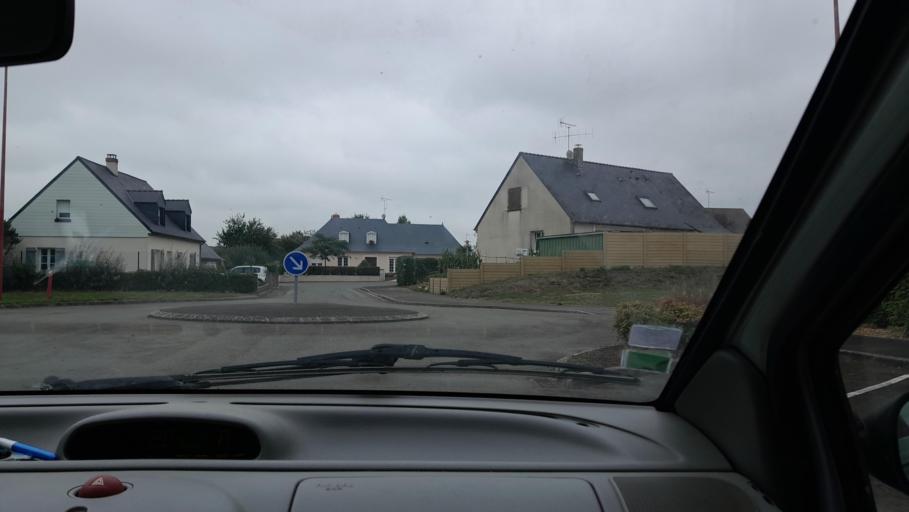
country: FR
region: Pays de la Loire
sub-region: Departement de la Mayenne
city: Cosse-le-Vivien
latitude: 47.9491
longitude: -0.9155
